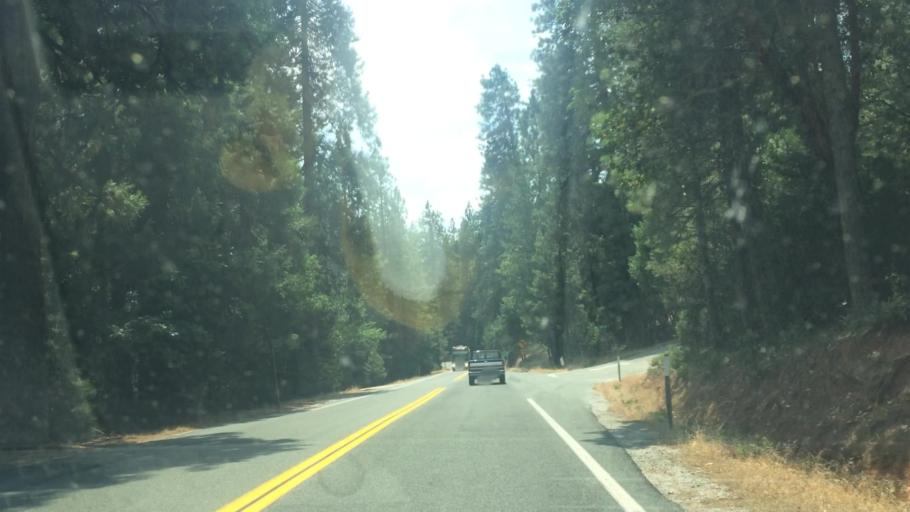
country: US
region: California
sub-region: Amador County
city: Pioneer
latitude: 38.4659
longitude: -120.5274
